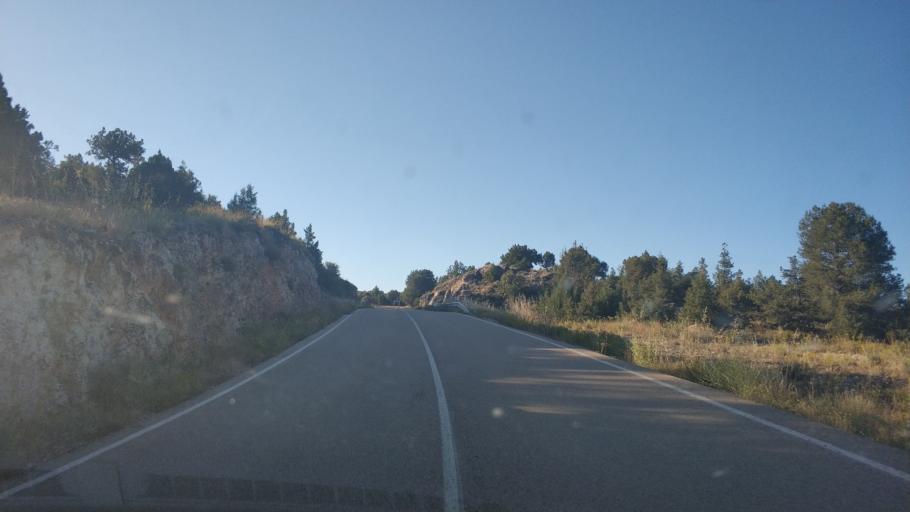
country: ES
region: Castille and Leon
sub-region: Provincia de Soria
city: Liceras
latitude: 41.4405
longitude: -3.2141
